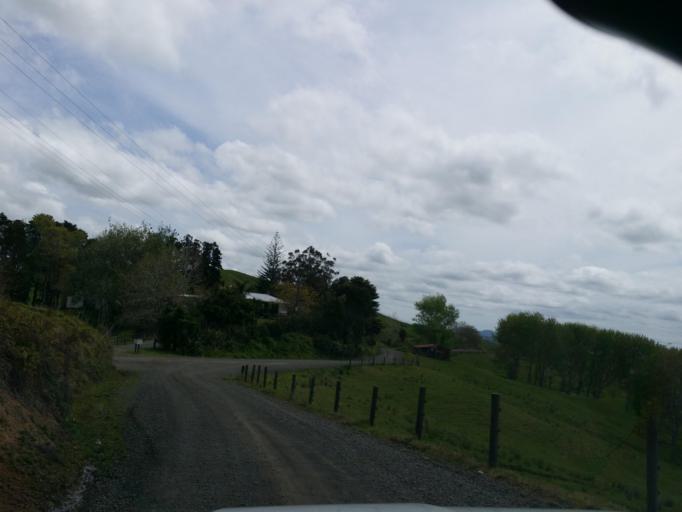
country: NZ
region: Northland
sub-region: Kaipara District
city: Dargaville
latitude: -35.9085
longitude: 174.0302
